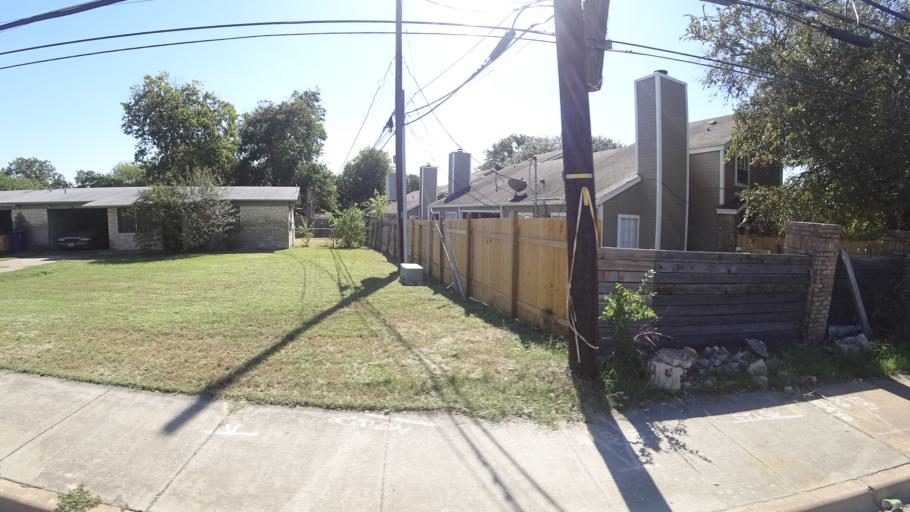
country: US
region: Texas
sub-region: Travis County
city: Austin
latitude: 30.3165
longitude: -97.7005
